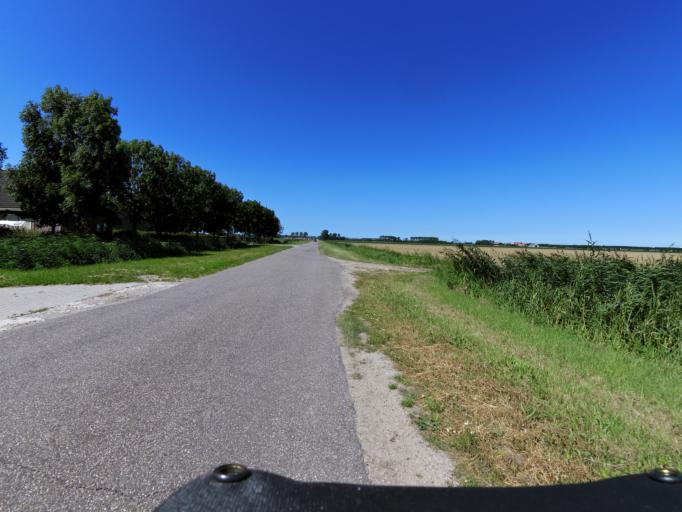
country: NL
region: South Holland
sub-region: Gemeente Goeree-Overflakkee
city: Dirksland
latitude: 51.7868
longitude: 4.0501
